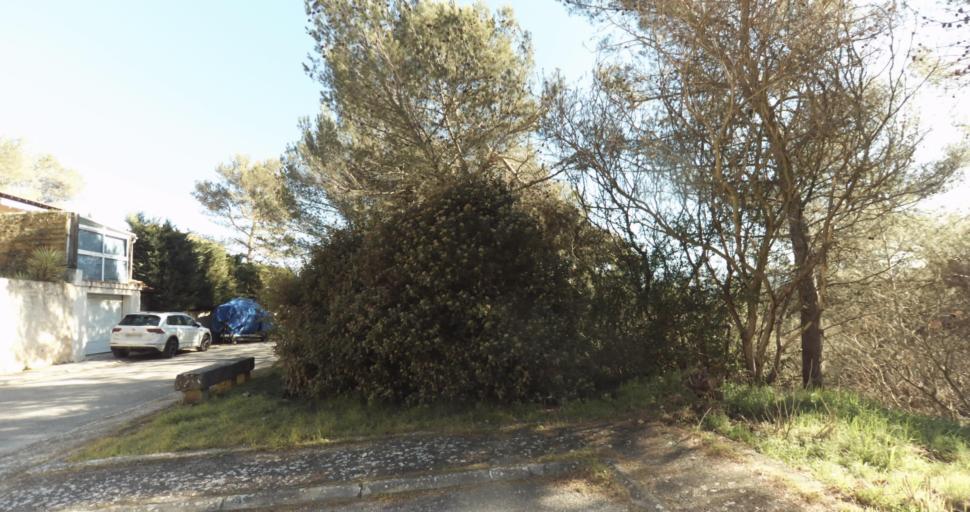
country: FR
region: Provence-Alpes-Cote d'Azur
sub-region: Departement des Bouches-du-Rhone
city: Peypin
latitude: 43.3878
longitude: 5.5660
